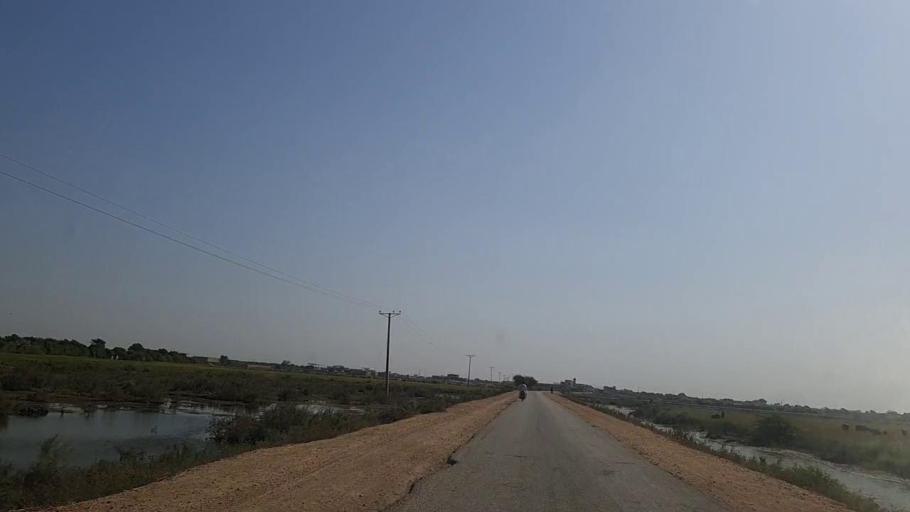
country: PK
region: Sindh
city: Mirpur Batoro
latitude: 24.6254
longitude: 68.2944
